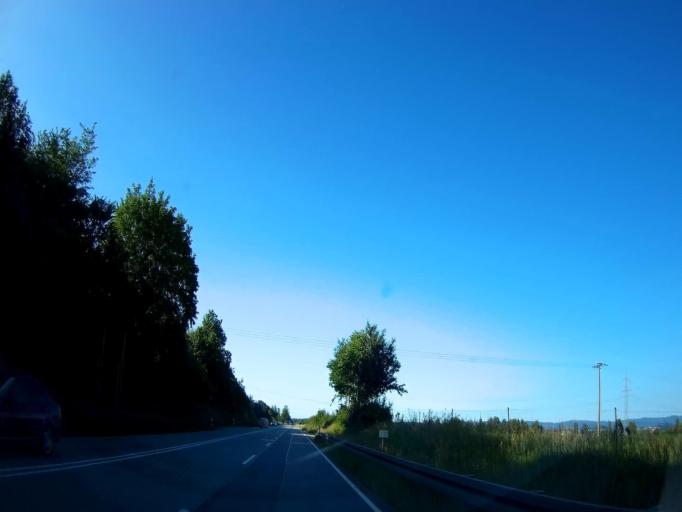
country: DE
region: Bavaria
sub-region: Lower Bavaria
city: Parkstetten
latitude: 48.9173
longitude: 12.6183
